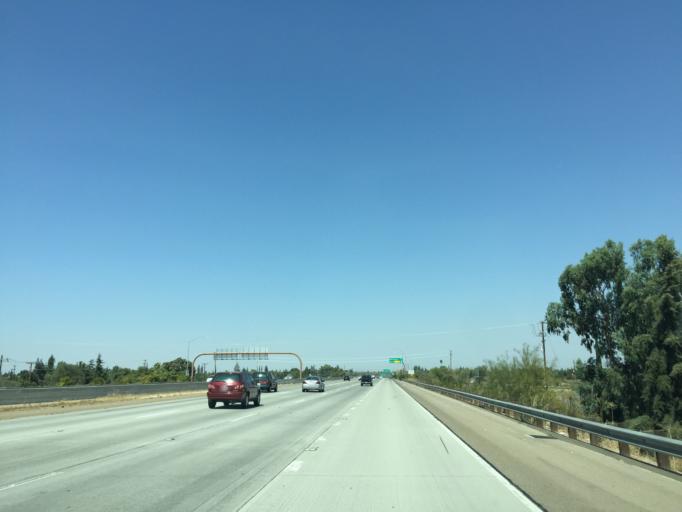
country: US
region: California
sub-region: Fresno County
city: Fresno
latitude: 36.7621
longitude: -119.7492
